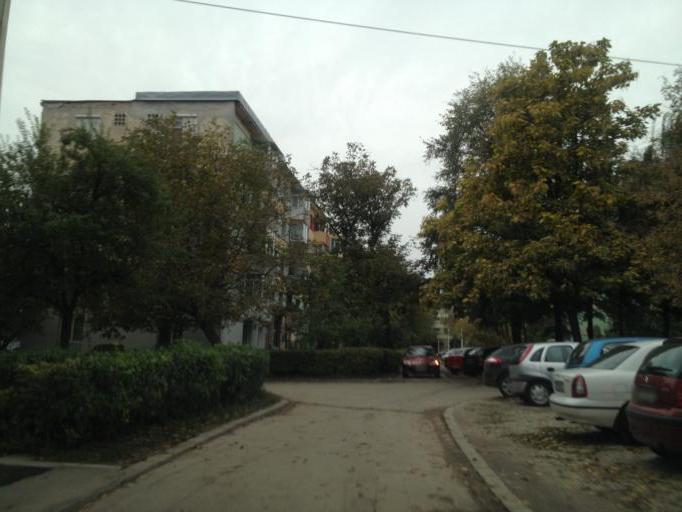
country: RO
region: Dolj
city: Craiova
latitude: 44.3272
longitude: 23.7822
